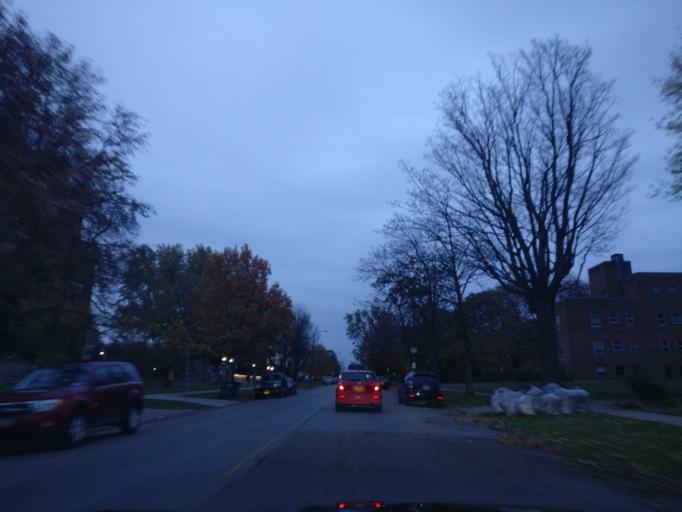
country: US
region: New York
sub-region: Erie County
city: Buffalo
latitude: 42.9154
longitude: -78.8722
